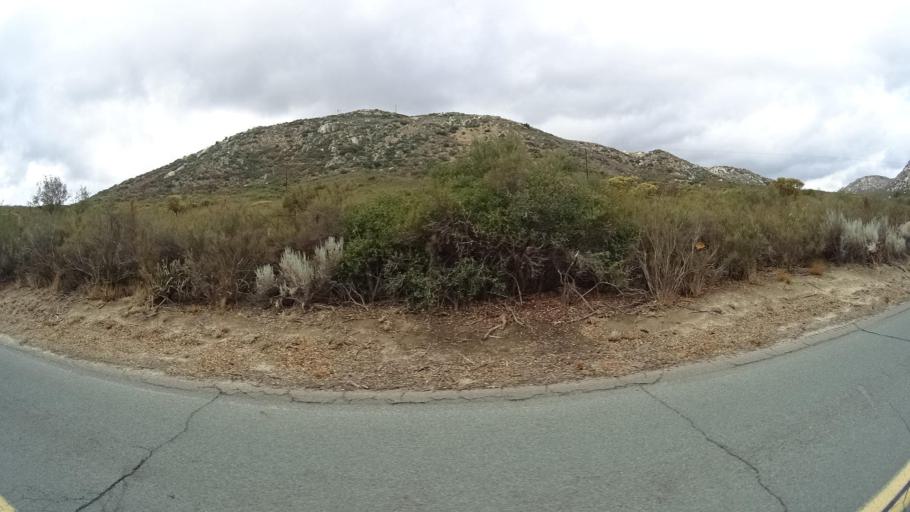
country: US
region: California
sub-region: San Diego County
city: Campo
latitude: 32.6819
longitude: -116.4305
